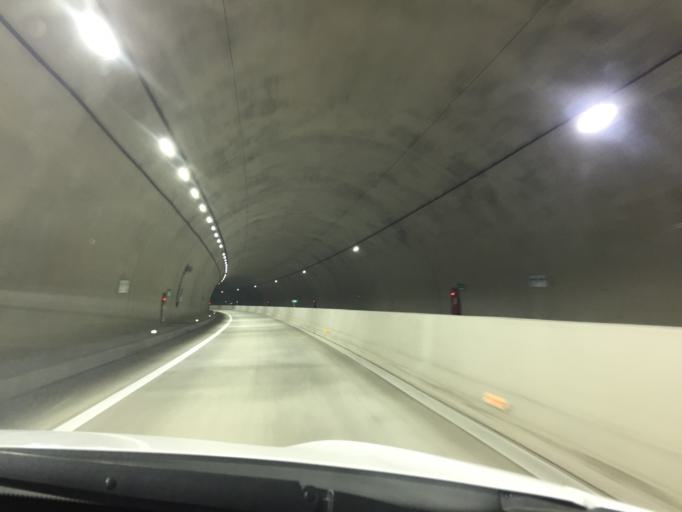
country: JP
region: Fukushima
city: Yanagawamachi-saiwaicho
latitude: 37.7545
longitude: 140.6584
